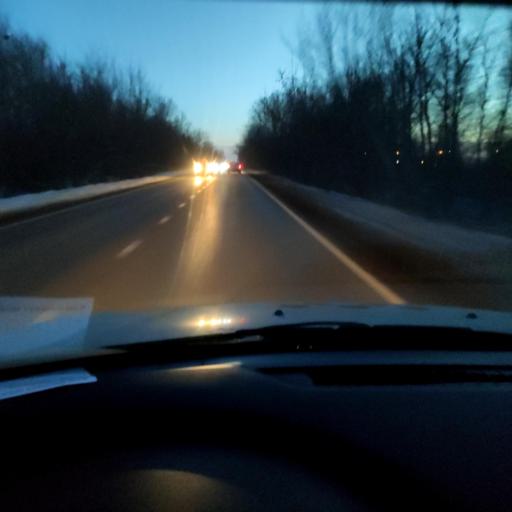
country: RU
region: Samara
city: Tol'yatti
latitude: 53.5485
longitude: 49.3935
